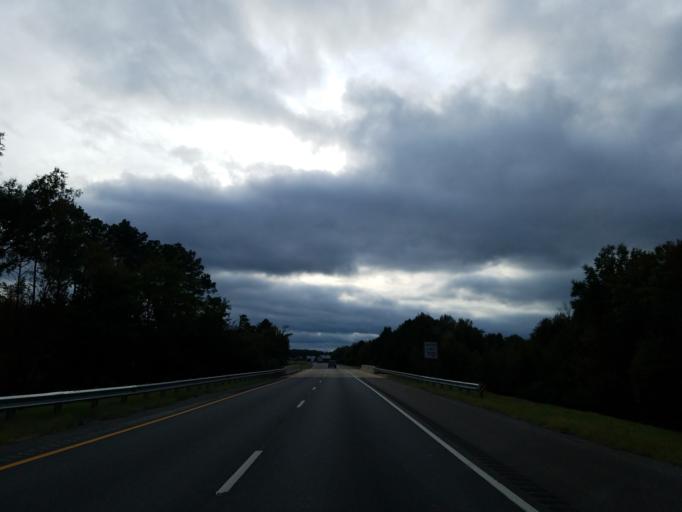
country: US
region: Alabama
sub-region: Tuscaloosa County
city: Tuscaloosa
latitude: 33.1499
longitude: -87.6092
